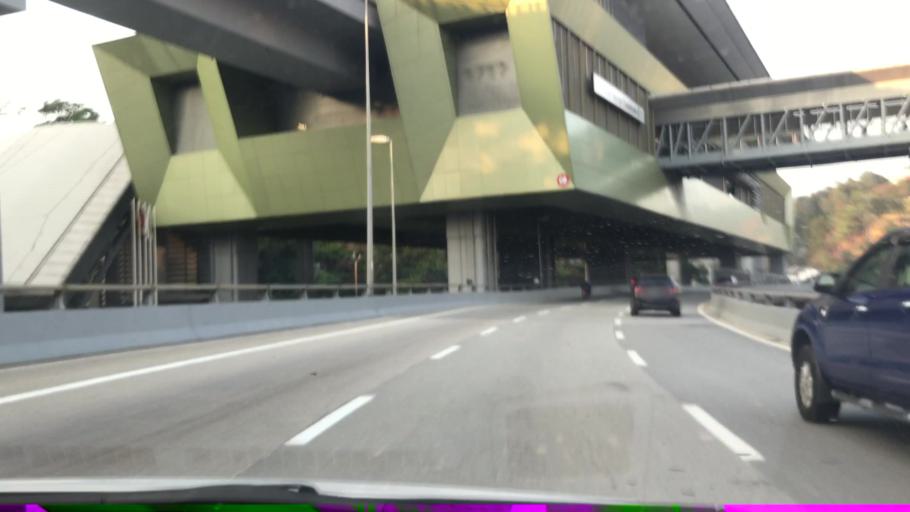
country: MY
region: Kuala Lumpur
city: Kuala Lumpur
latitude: 3.1439
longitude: 101.6632
